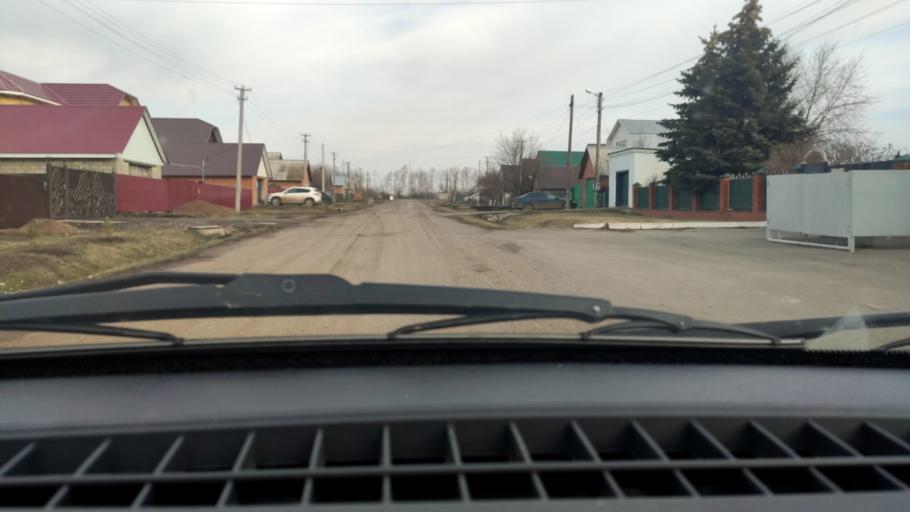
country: RU
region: Bashkortostan
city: Davlekanovo
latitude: 54.2320
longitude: 55.0289
